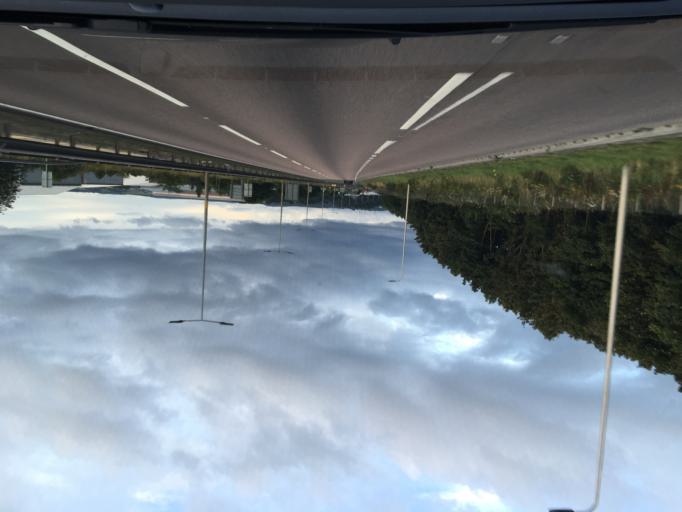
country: GB
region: Scotland
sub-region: Highland
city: Inverness
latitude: 57.4908
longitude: -4.2134
